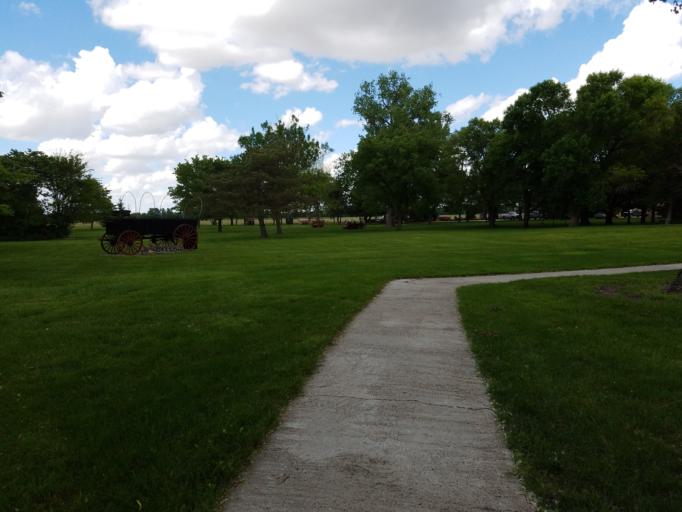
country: US
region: Nebraska
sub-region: Buffalo County
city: Kearney
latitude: 40.6435
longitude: -99.0056
